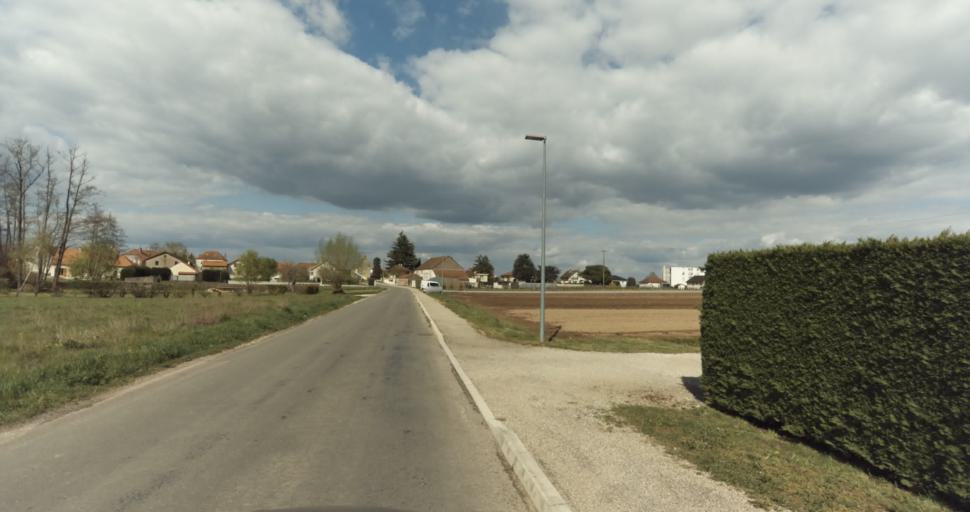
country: FR
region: Bourgogne
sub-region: Departement de la Cote-d'Or
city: Auxonne
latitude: 47.1915
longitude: 5.4023
